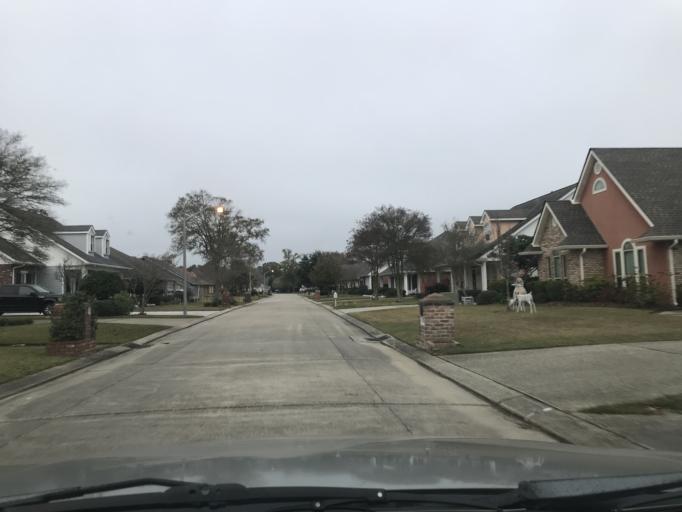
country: US
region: Louisiana
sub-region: Jefferson Parish
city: Woodmere
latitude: 29.8699
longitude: -90.0922
